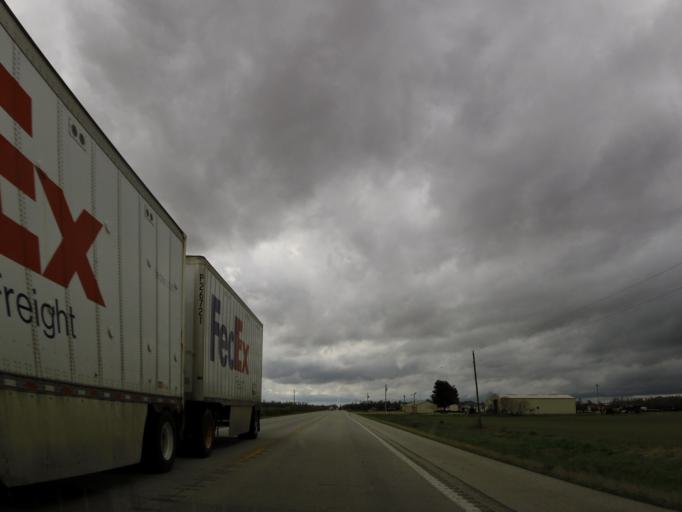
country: US
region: Missouri
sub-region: Butler County
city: Poplar Bluff
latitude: 36.6192
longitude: -90.5204
